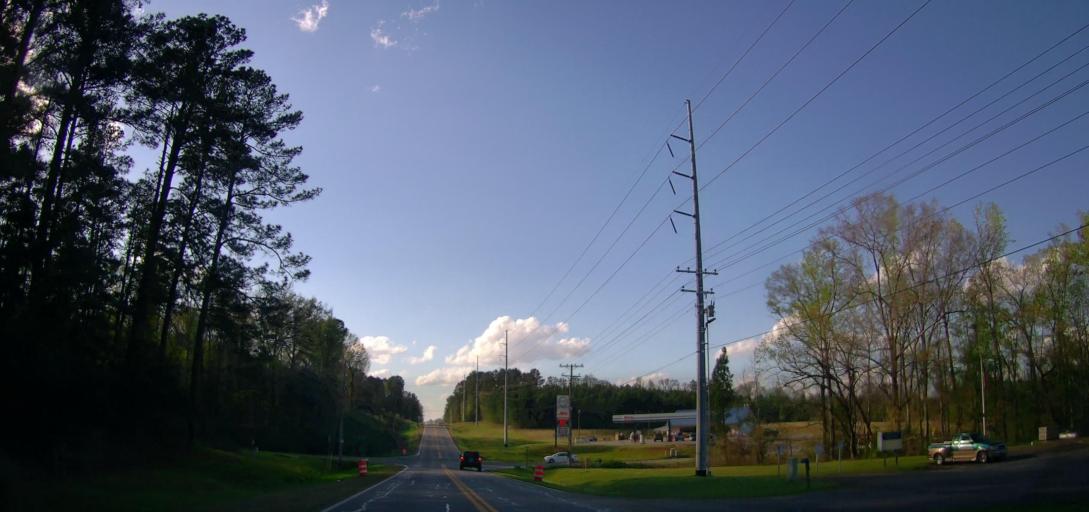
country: US
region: Georgia
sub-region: Baldwin County
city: Milledgeville
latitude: 33.1535
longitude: -83.3469
